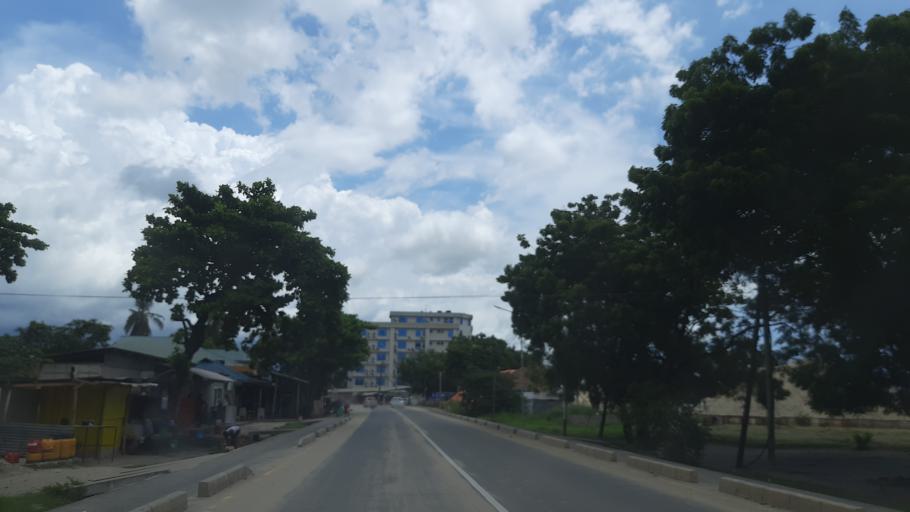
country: TZ
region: Dar es Salaam
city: Magomeni
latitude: -6.7702
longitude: 39.2285
